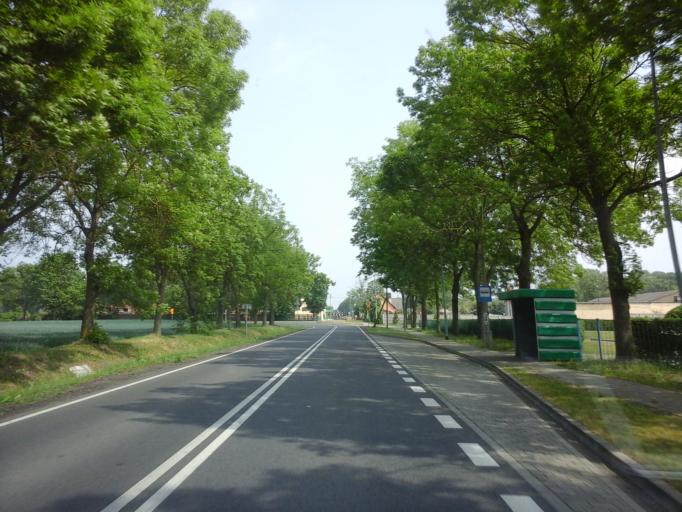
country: PL
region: West Pomeranian Voivodeship
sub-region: Powiat choszczenski
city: Pelczyce
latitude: 53.1001
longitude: 15.3384
